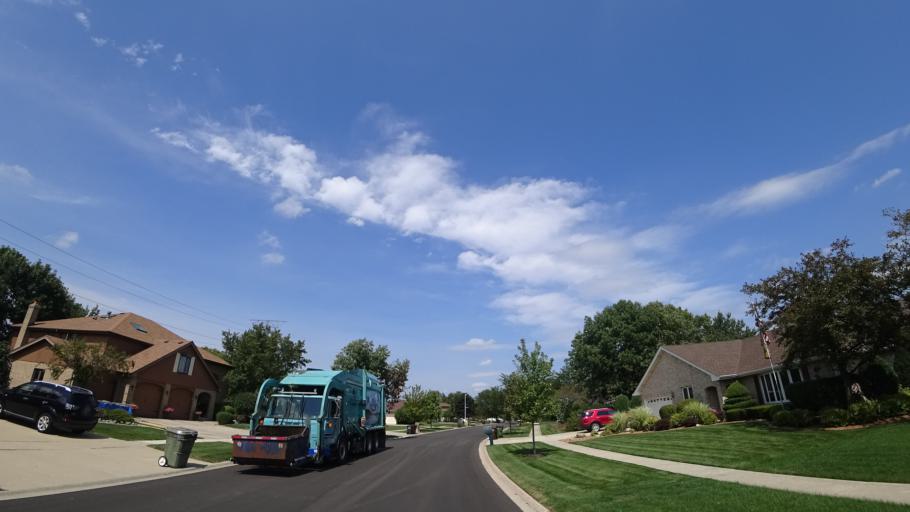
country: US
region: Illinois
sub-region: Cook County
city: Orland Hills
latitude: 41.5673
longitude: -87.8167
